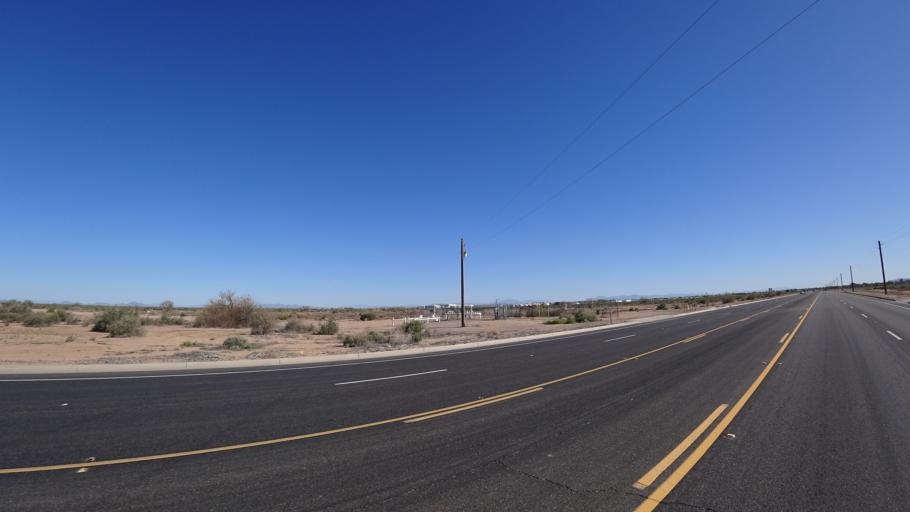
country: US
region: Arizona
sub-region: Maricopa County
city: Sun Lakes
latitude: 33.2193
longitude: -111.9122
